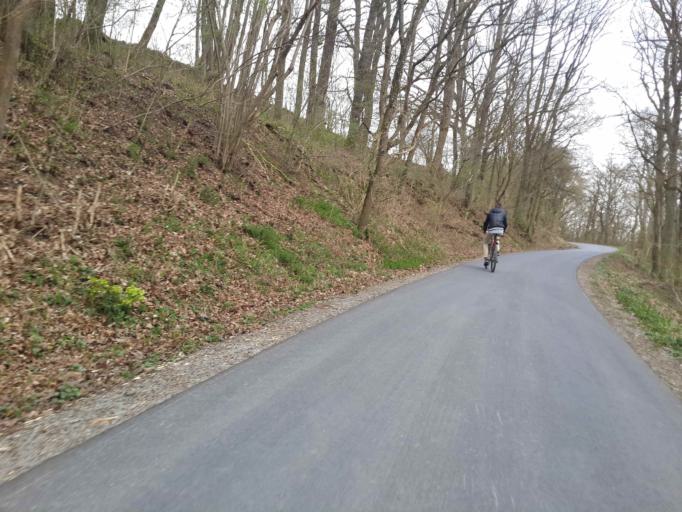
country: DE
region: Baden-Wuerttemberg
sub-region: Karlsruhe Region
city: Rosenberg
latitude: 49.4505
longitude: 9.4598
